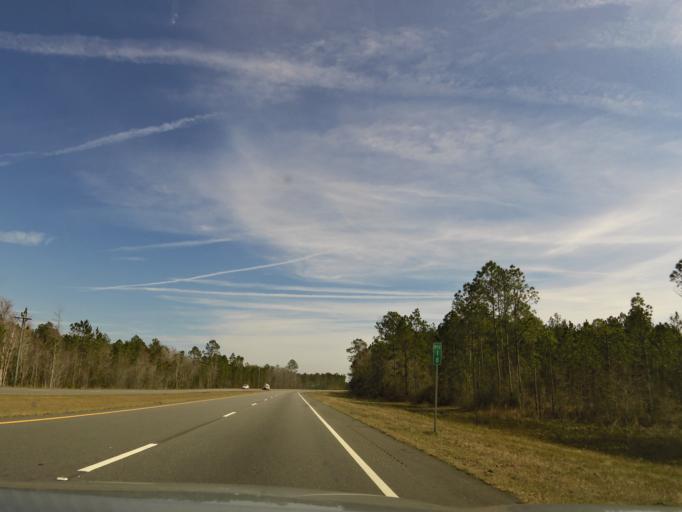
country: US
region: Georgia
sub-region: Brantley County
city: Nahunta
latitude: 31.2139
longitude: -81.9133
